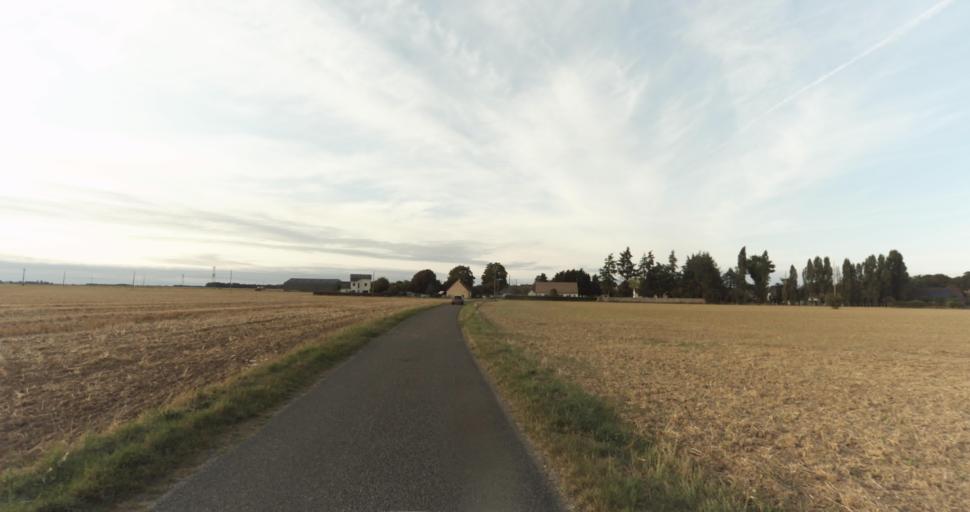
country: FR
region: Haute-Normandie
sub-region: Departement de l'Eure
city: Marcilly-sur-Eure
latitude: 48.8451
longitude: 1.2727
